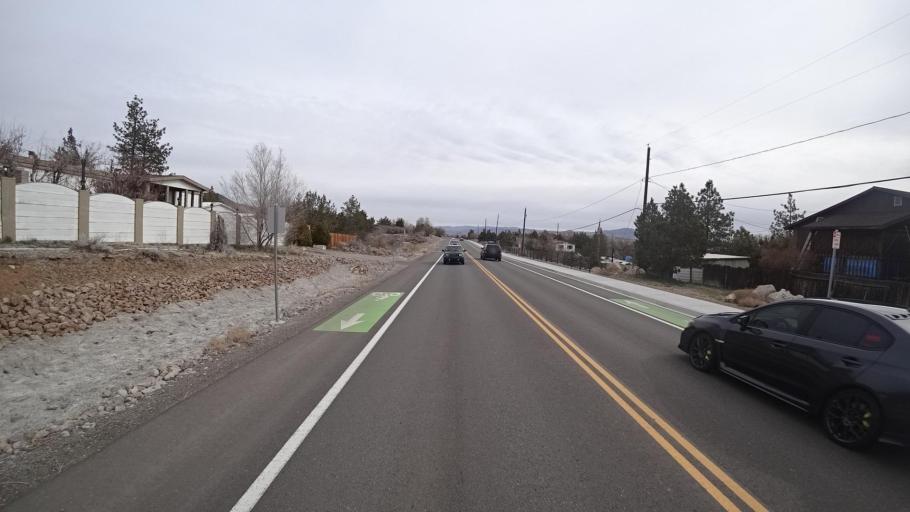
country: US
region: Nevada
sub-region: Washoe County
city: Sun Valley
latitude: 39.6114
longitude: -119.7756
